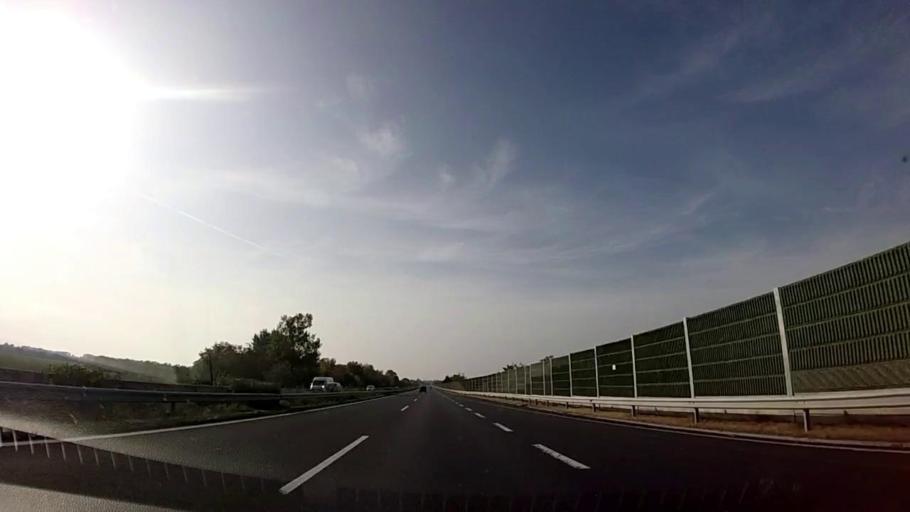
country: HU
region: Somogy
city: Balatonszabadi
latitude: 46.9516
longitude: 18.1518
